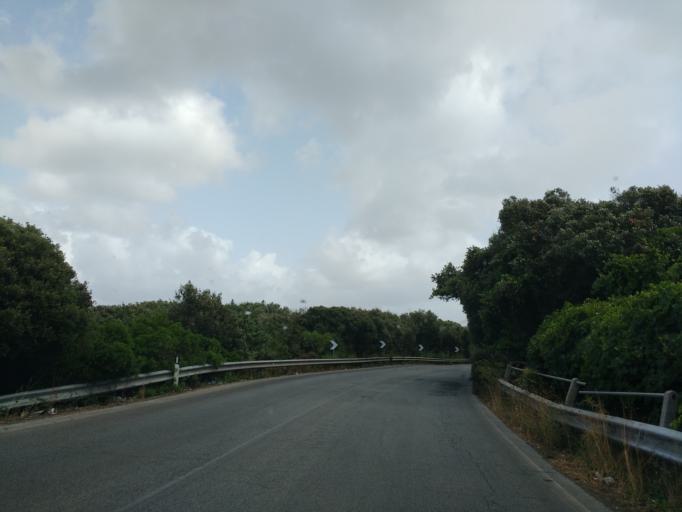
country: IT
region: Latium
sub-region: Citta metropolitana di Roma Capitale
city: Torvaianica
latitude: 41.6678
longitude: 12.4021
